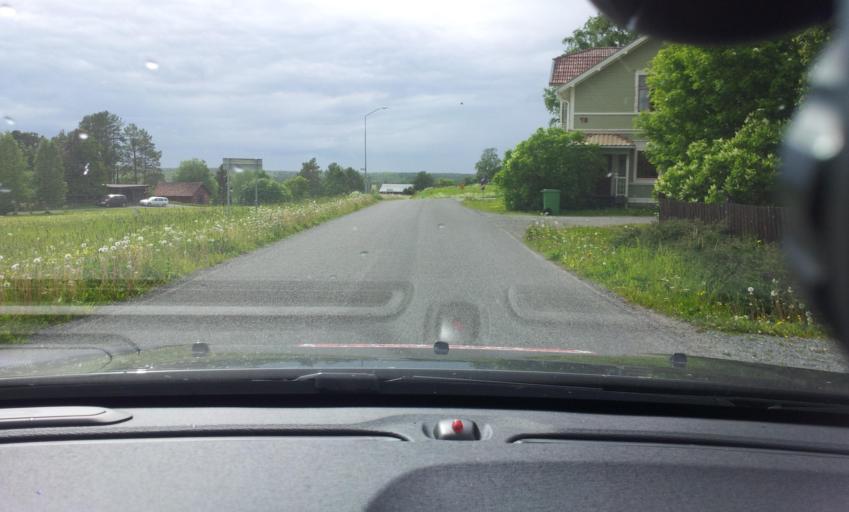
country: SE
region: Jaemtland
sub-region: OEstersunds Kommun
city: Brunflo
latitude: 63.0264
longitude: 14.7933
